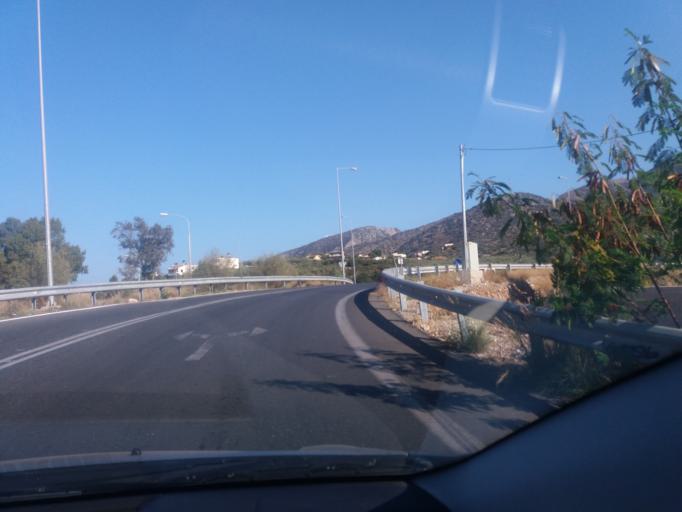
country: GR
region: Crete
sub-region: Nomos Lasithiou
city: Sision
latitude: 35.2914
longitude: 25.5114
